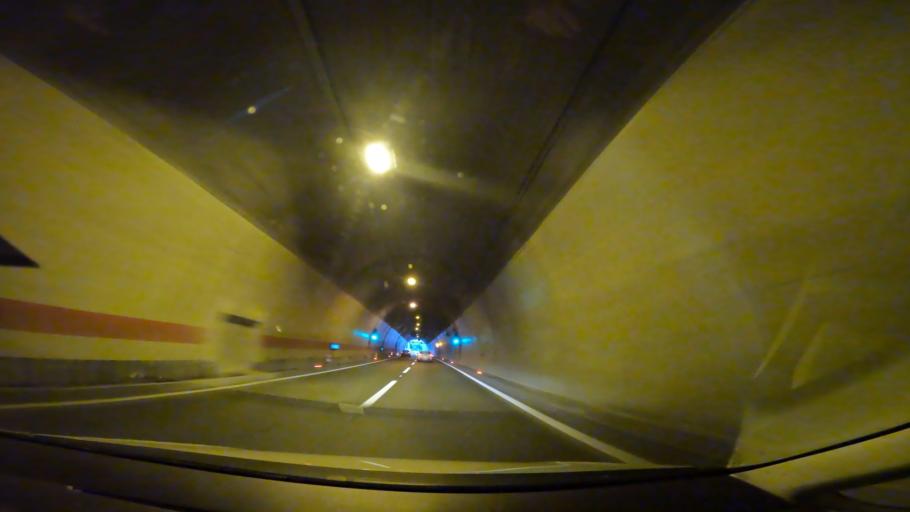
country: HR
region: Primorsko-Goranska
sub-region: Grad Delnice
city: Delnice
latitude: 45.3697
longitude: 14.7660
